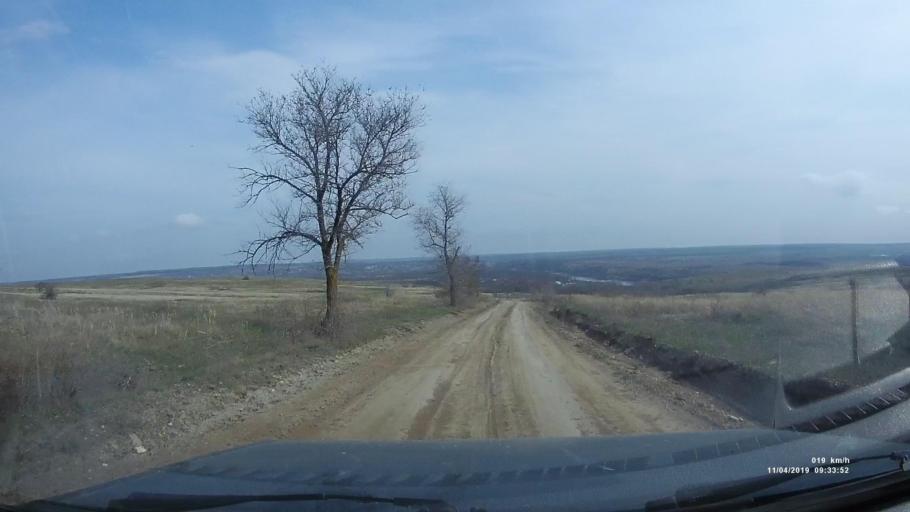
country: RU
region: Rostov
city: Staraya Stanitsa
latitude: 48.2673
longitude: 40.3680
